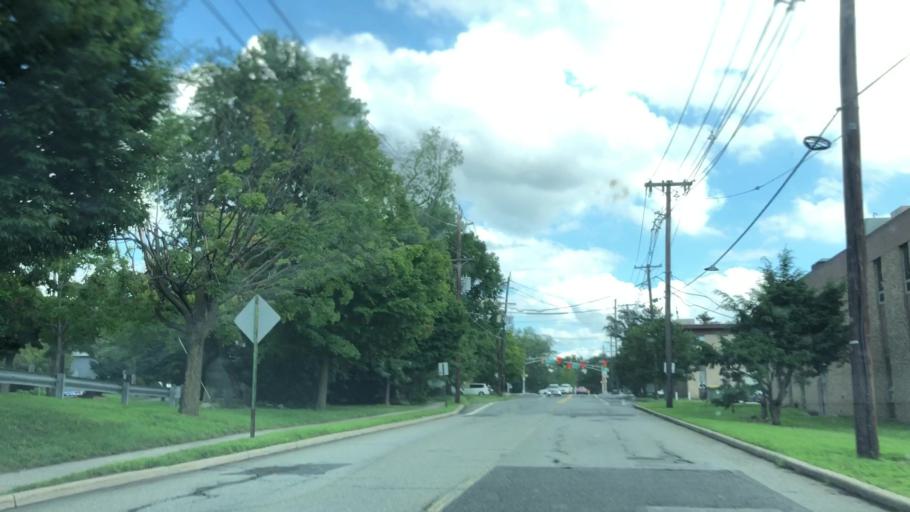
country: US
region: New Jersey
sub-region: Bergen County
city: Rochelle Park
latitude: 40.9117
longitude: -74.0741
